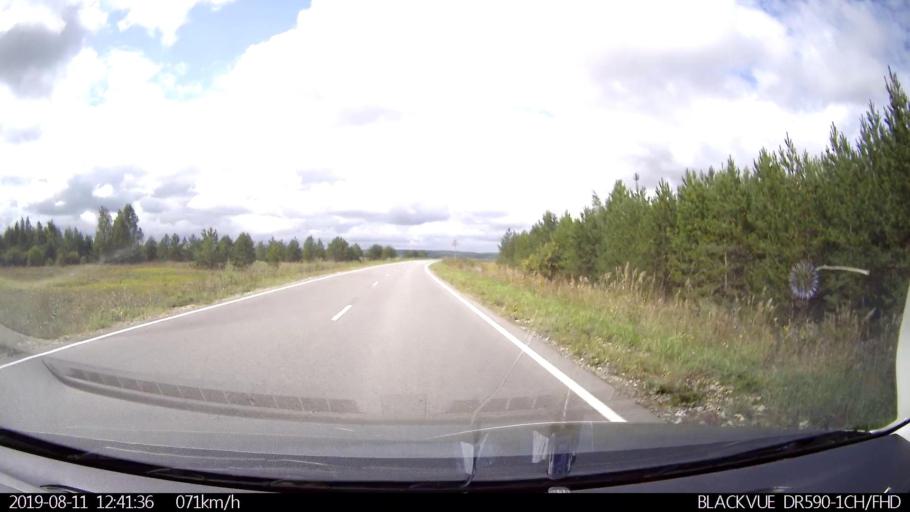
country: RU
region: Ulyanovsk
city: Ignatovka
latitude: 53.8420
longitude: 47.7630
